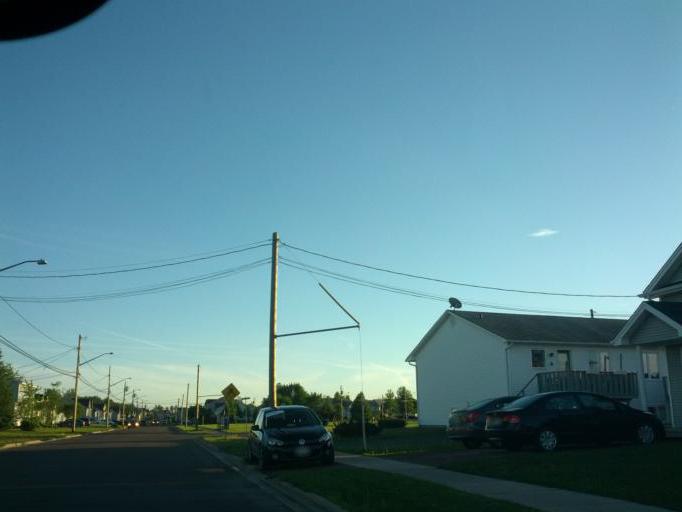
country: CA
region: New Brunswick
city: Moncton
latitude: 46.1201
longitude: -64.8490
